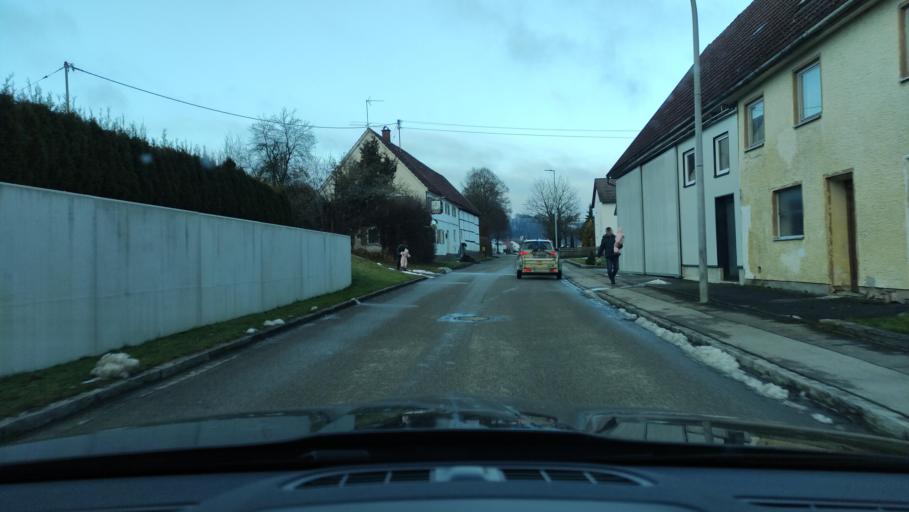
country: DE
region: Bavaria
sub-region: Swabia
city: Deisenhausen
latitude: 48.2956
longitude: 10.3562
